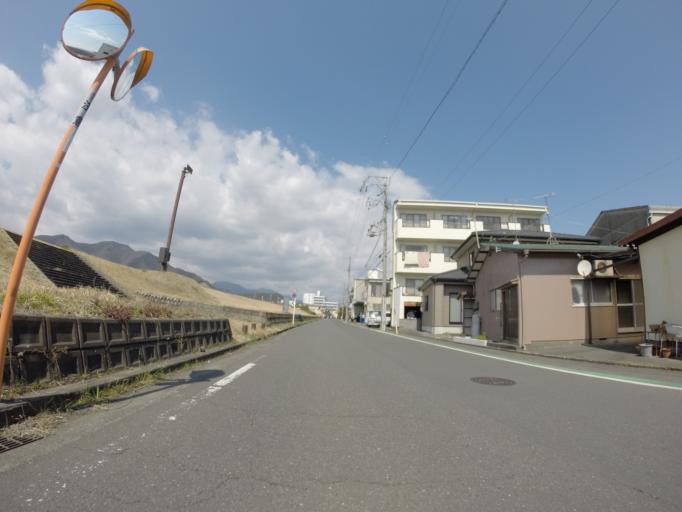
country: JP
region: Shizuoka
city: Shizuoka-shi
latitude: 34.9886
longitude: 138.3643
